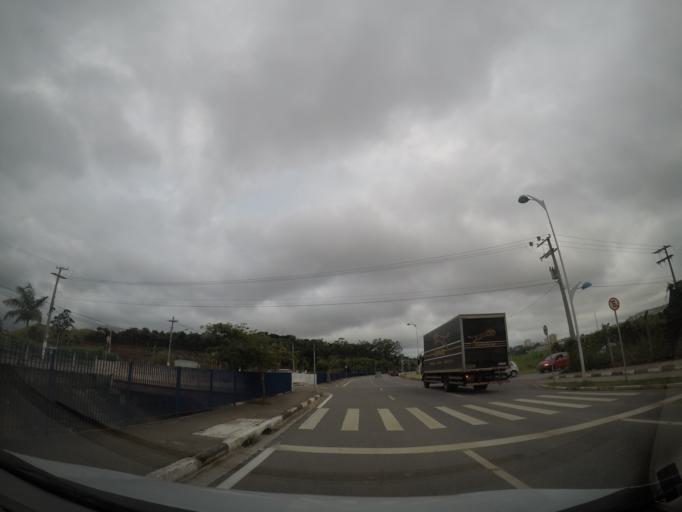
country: BR
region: Sao Paulo
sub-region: Aruja
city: Aruja
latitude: -23.4007
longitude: -46.3571
